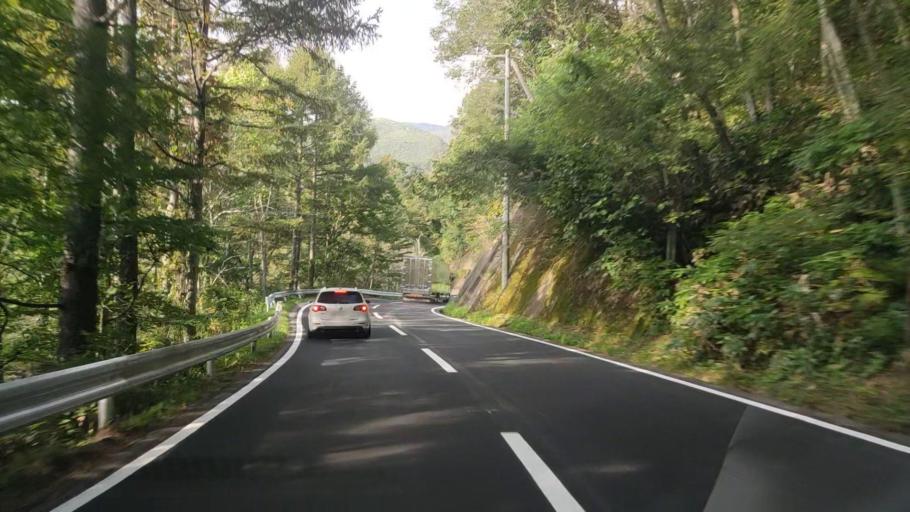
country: JP
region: Nagano
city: Ueda
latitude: 36.4941
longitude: 138.3889
